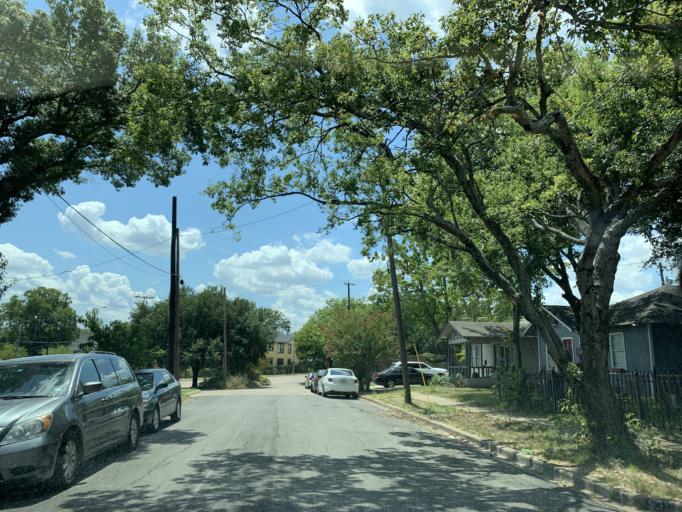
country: US
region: Texas
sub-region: Dallas County
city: Dallas
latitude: 32.7512
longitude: -96.8390
